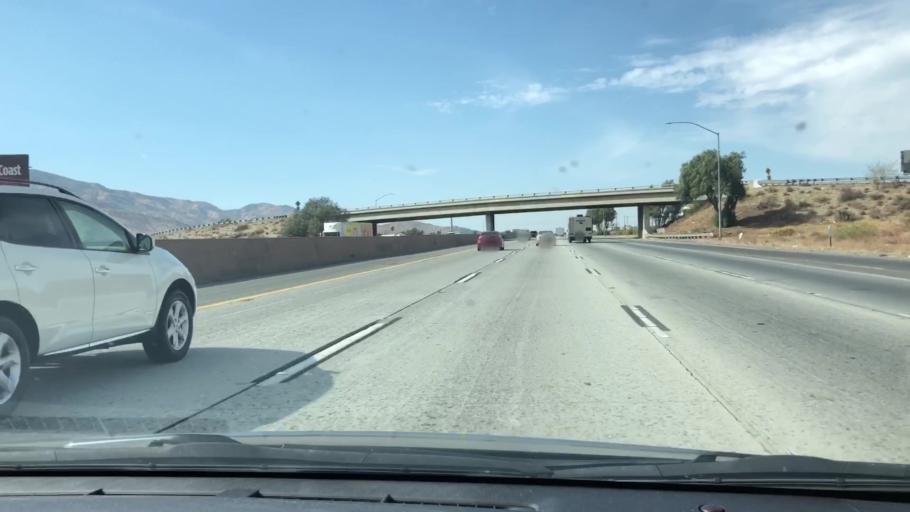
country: US
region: California
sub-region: Riverside County
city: Cabazon
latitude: 33.9192
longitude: -116.7758
